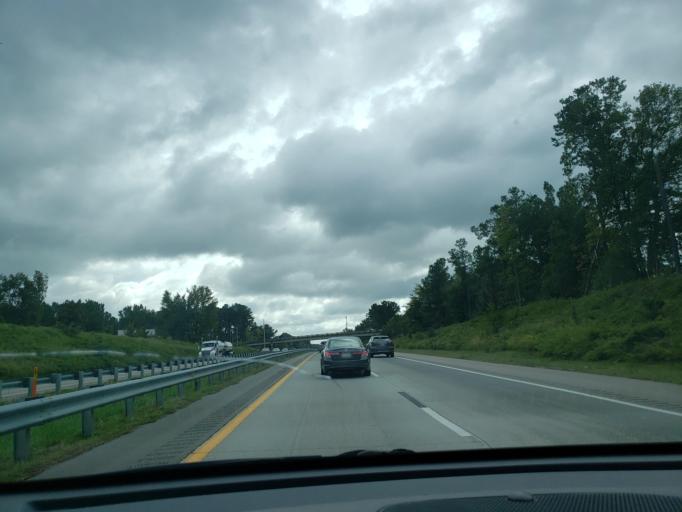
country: US
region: North Carolina
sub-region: Vance County
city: Henderson
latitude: 36.4090
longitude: -78.3252
